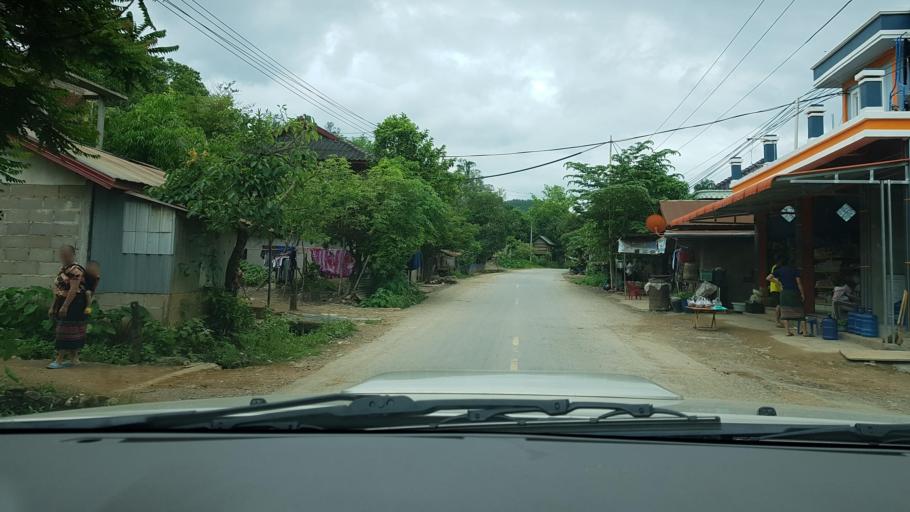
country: LA
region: Loungnamtha
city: Muang Nale
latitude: 20.2530
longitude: 101.5851
